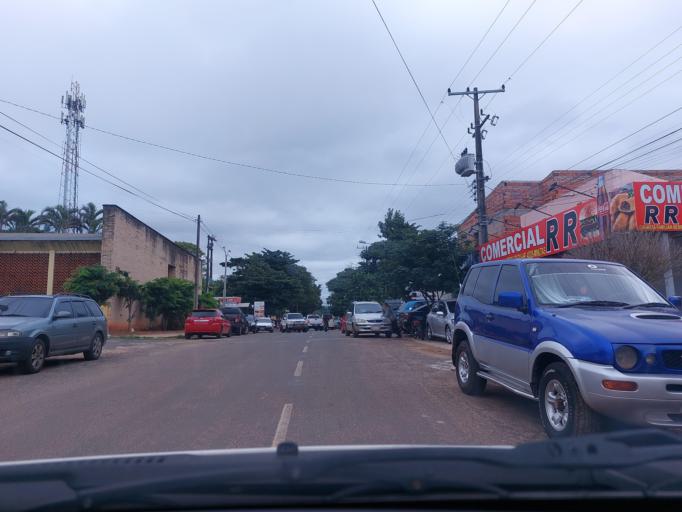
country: PY
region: San Pedro
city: Guayaybi
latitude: -24.6618
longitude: -56.4419
